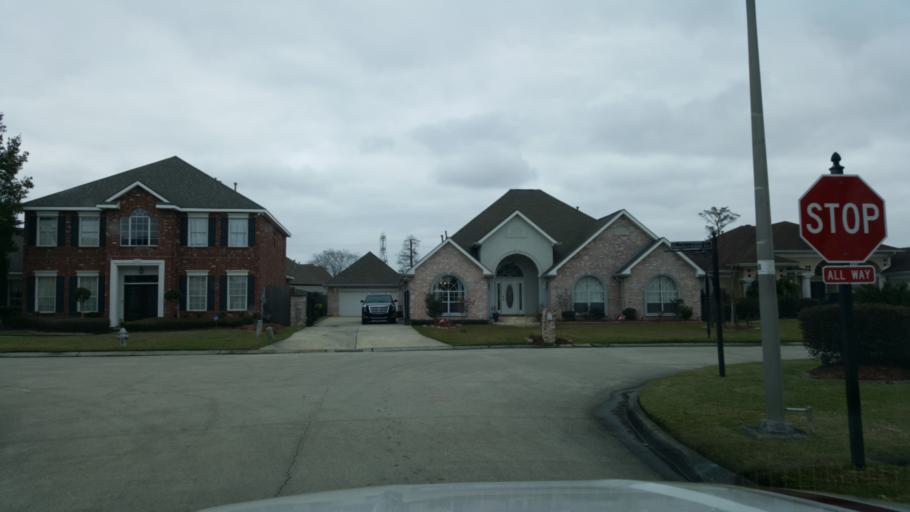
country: US
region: Louisiana
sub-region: Jefferson Parish
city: Woodmere
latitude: 29.8781
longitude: -90.0798
